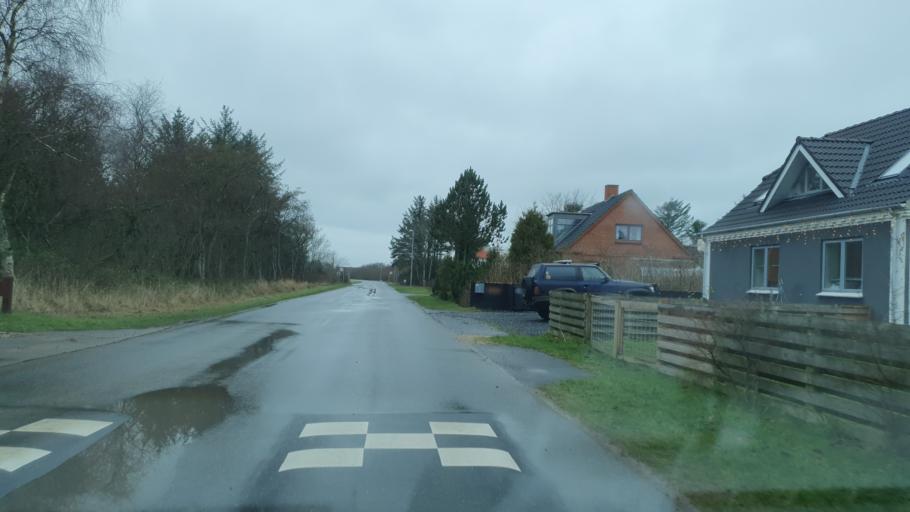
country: DK
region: North Denmark
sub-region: Jammerbugt Kommune
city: Fjerritslev
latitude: 57.1334
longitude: 9.1309
